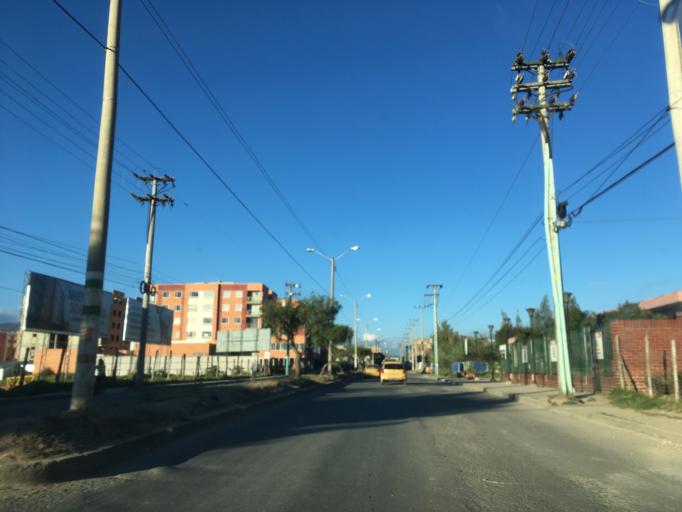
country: CO
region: Boyaca
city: Sogamoso
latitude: 5.7033
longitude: -72.9372
